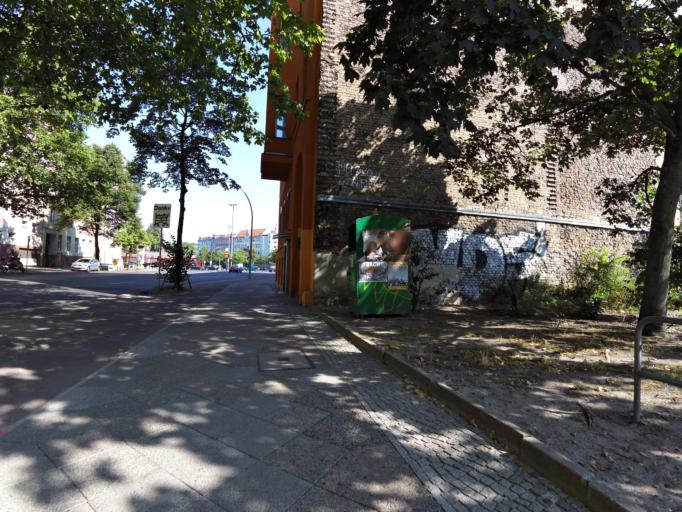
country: DE
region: Berlin
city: Tiergarten Bezirk
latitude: 52.5227
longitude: 13.3567
